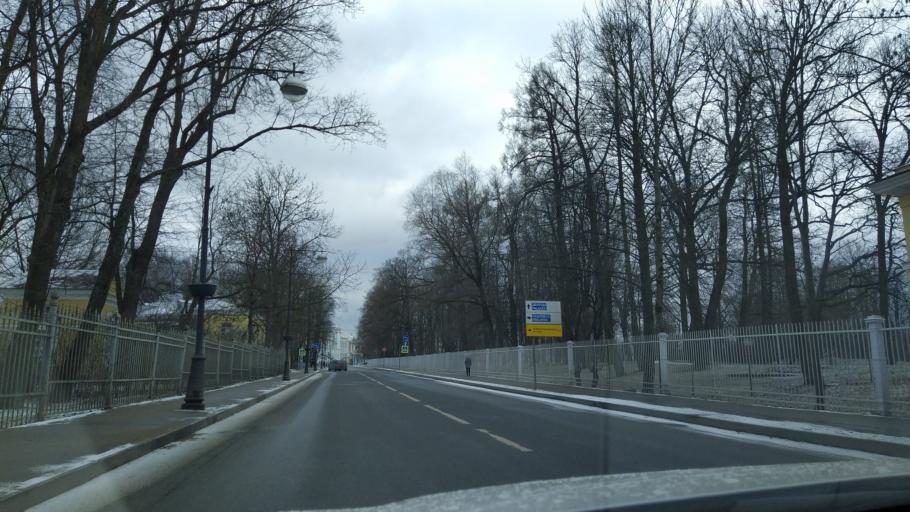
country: RU
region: St.-Petersburg
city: Pushkin
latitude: 59.7205
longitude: 30.3959
